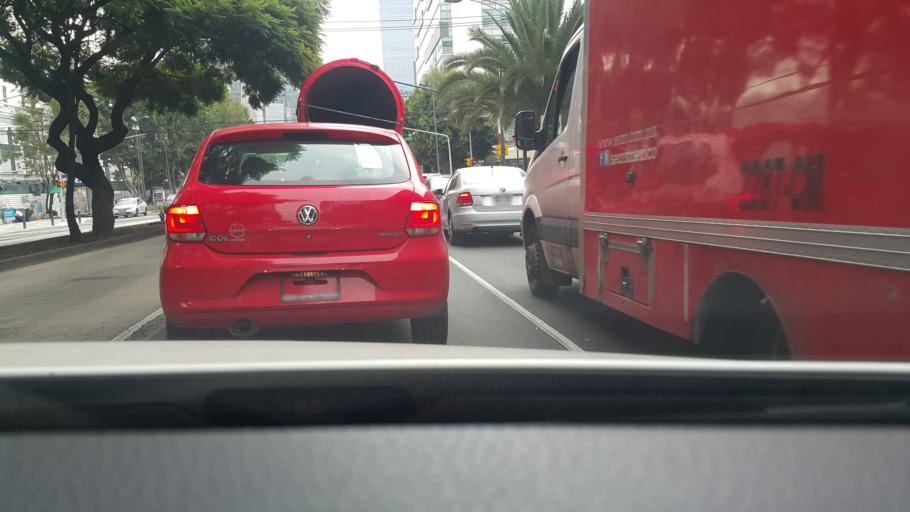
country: MX
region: Mexico City
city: Alvaro Obregon
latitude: 19.3654
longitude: -99.1815
